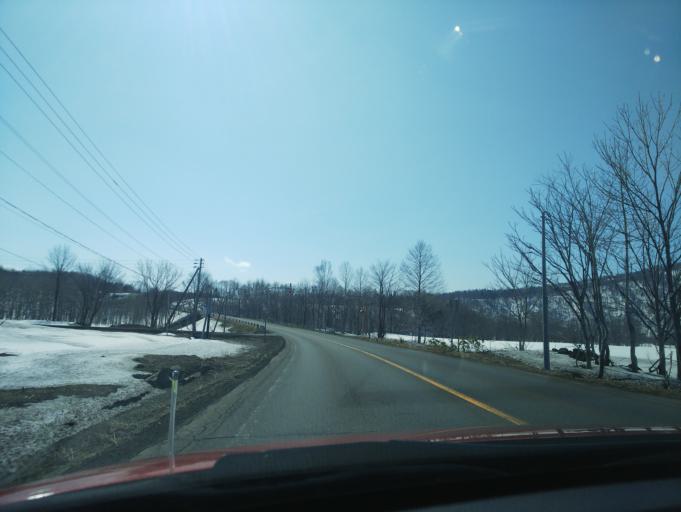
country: JP
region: Hokkaido
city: Nayoro
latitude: 44.6472
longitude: 142.2640
